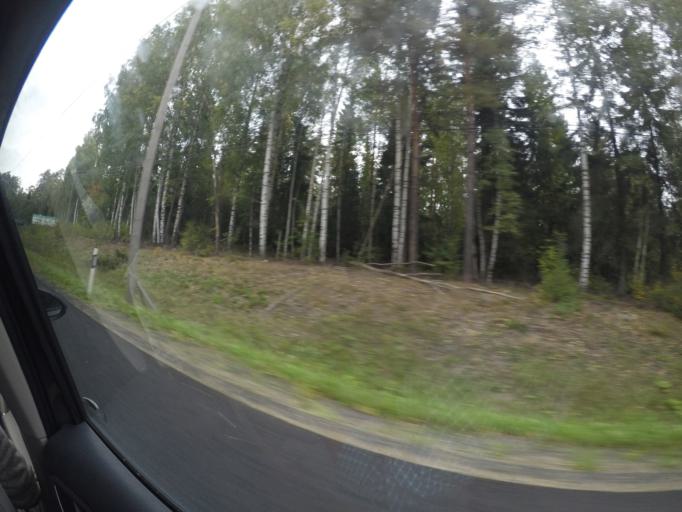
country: FI
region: Pirkanmaa
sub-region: Tampere
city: Kangasala
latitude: 61.4459
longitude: 24.1098
